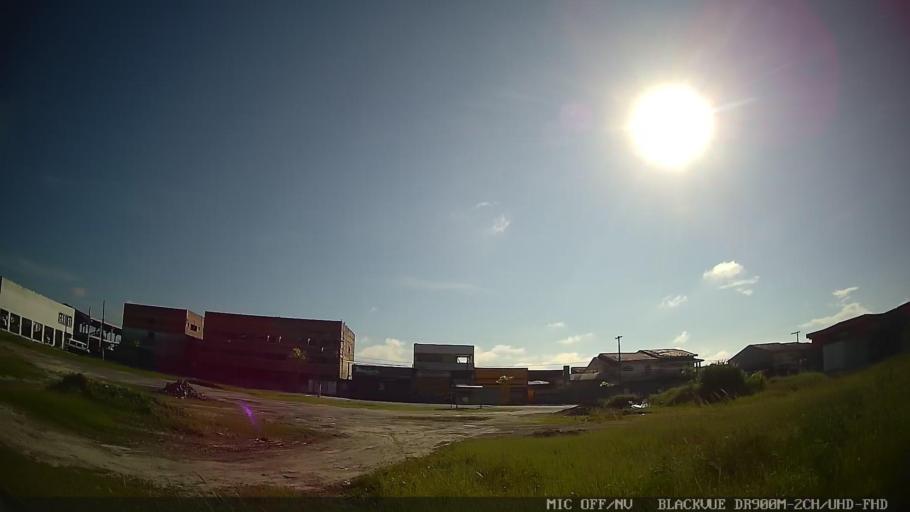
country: BR
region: Sao Paulo
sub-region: Peruibe
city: Peruibe
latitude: -24.2781
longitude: -46.9491
